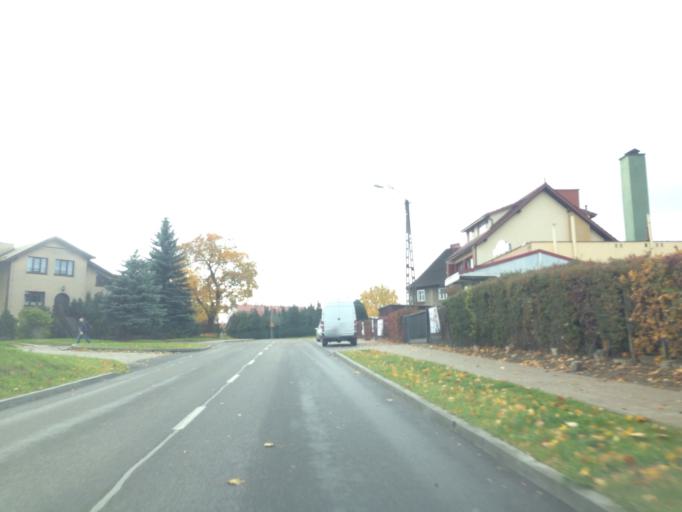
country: PL
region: Pomeranian Voivodeship
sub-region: Powiat tczewski
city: Tczew
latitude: 54.0796
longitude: 18.8006
